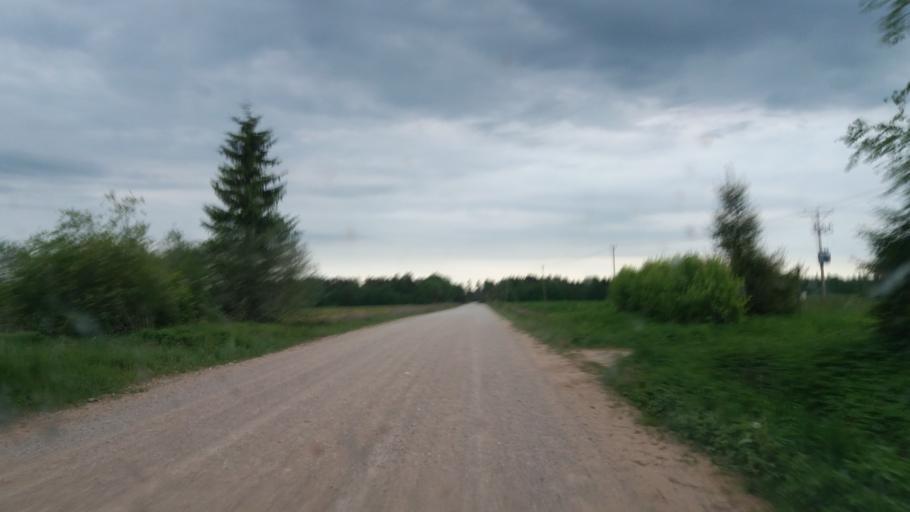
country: LV
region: Kuldigas Rajons
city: Kuldiga
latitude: 57.2183
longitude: 22.0839
